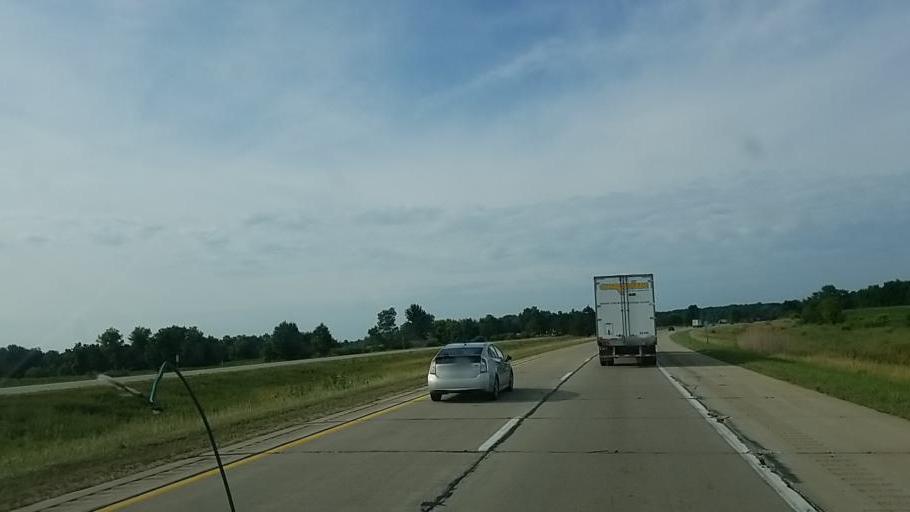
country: US
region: Michigan
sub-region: Eaton County
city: Charlotte
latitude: 42.5301
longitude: -84.8216
